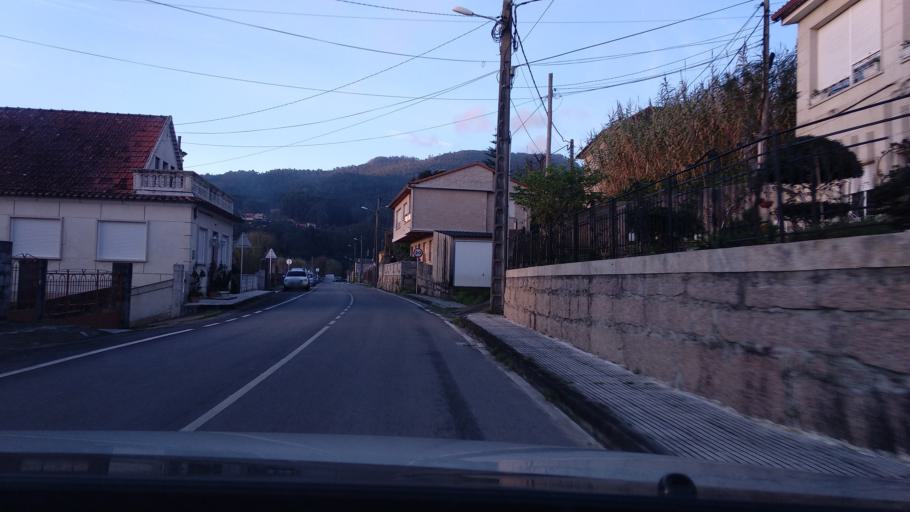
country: ES
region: Galicia
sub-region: Provincia de Pontevedra
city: Moana
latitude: 42.2979
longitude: -8.7242
